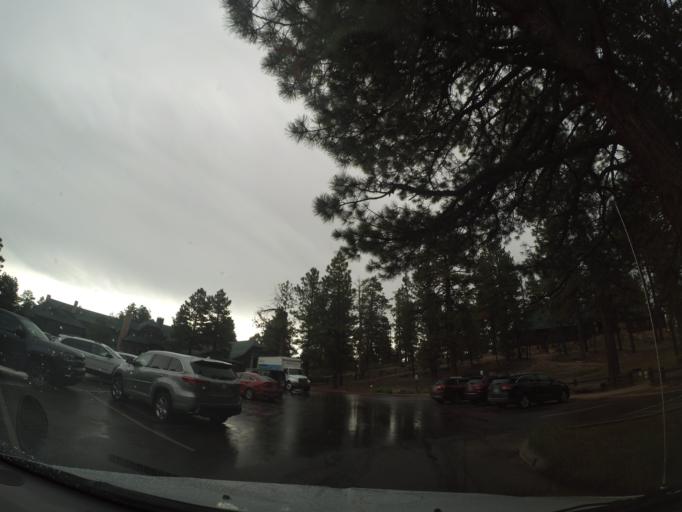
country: US
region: Utah
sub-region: Garfield County
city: Panguitch
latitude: 37.6273
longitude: -112.1689
